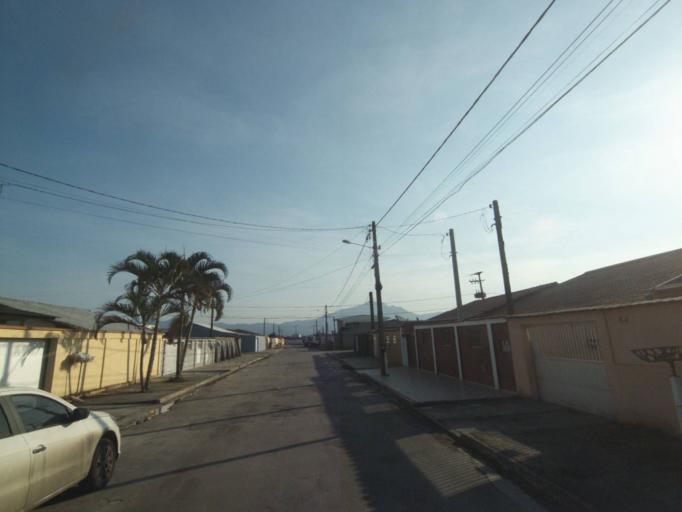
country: BR
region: Parana
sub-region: Paranagua
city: Paranagua
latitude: -25.5591
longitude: -48.5611
